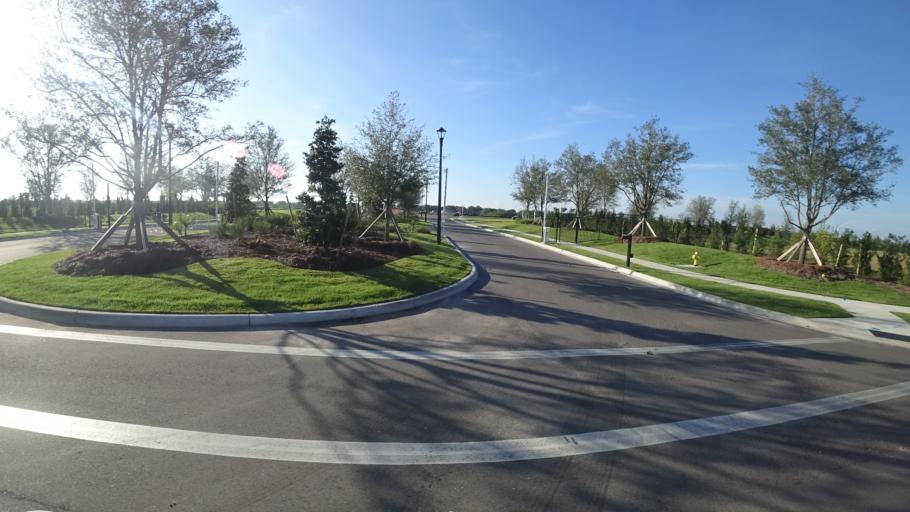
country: US
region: Florida
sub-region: Sarasota County
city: The Meadows
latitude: 27.4514
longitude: -82.3620
